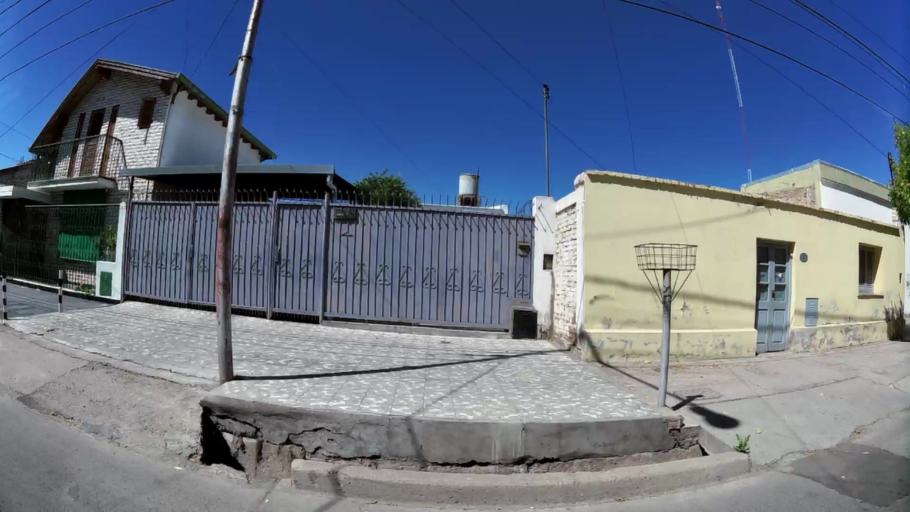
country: AR
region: Mendoza
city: Las Heras
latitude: -32.8472
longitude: -68.8426
